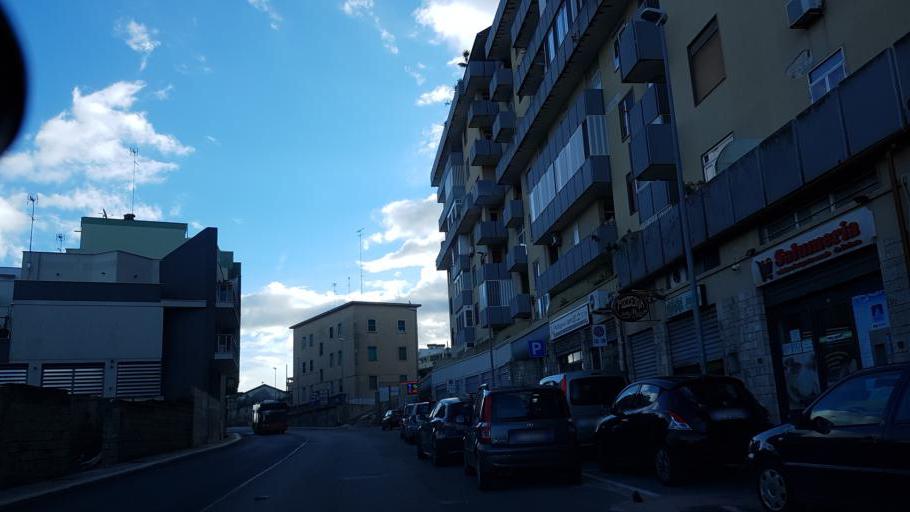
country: IT
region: Apulia
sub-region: Provincia di Brindisi
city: Brindisi
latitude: 40.6376
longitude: 17.9294
